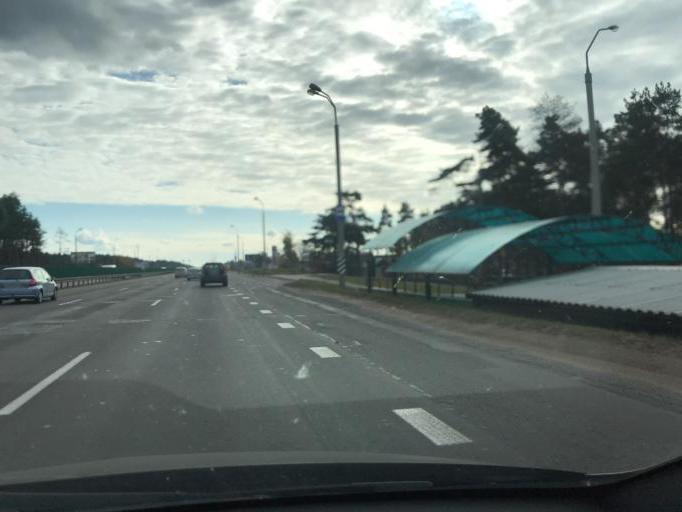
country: BY
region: Minsk
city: Vyaliki Trastsyanets
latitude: 53.9162
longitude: 27.6831
